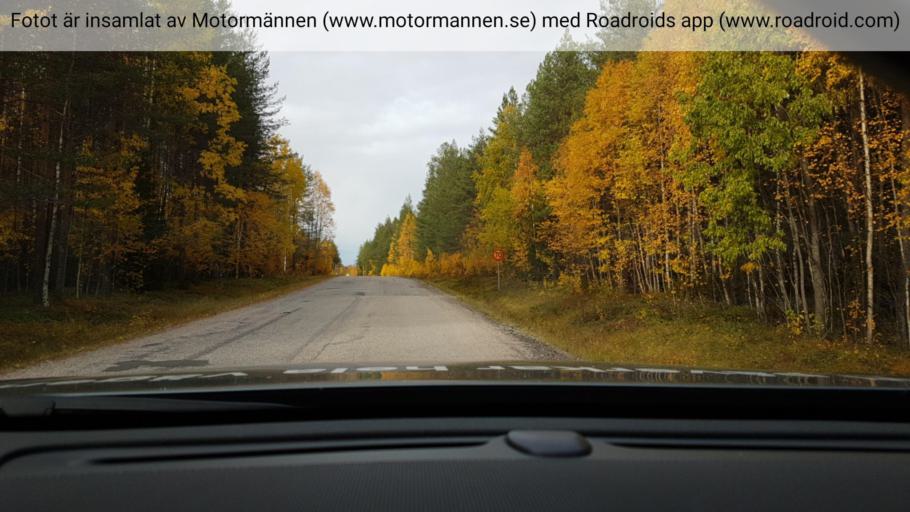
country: SE
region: Norrbotten
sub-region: Overkalix Kommun
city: OEverkalix
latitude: 66.2486
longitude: 23.1359
